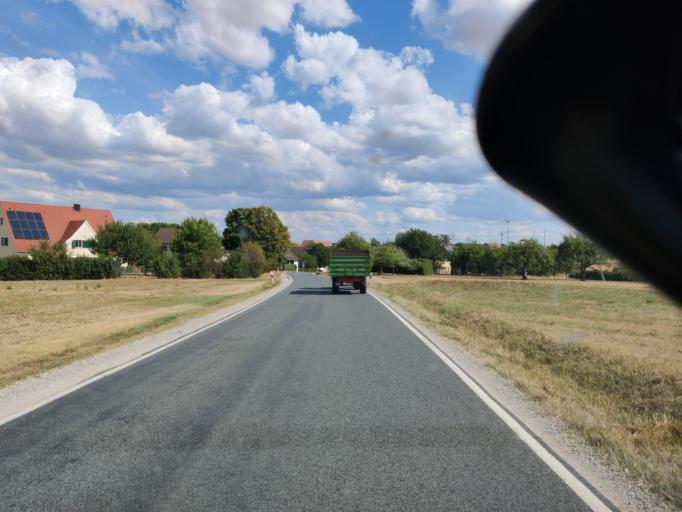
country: DE
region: Bavaria
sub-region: Regierungsbezirk Mittelfranken
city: Thalmassing
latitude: 49.0709
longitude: 11.2204
